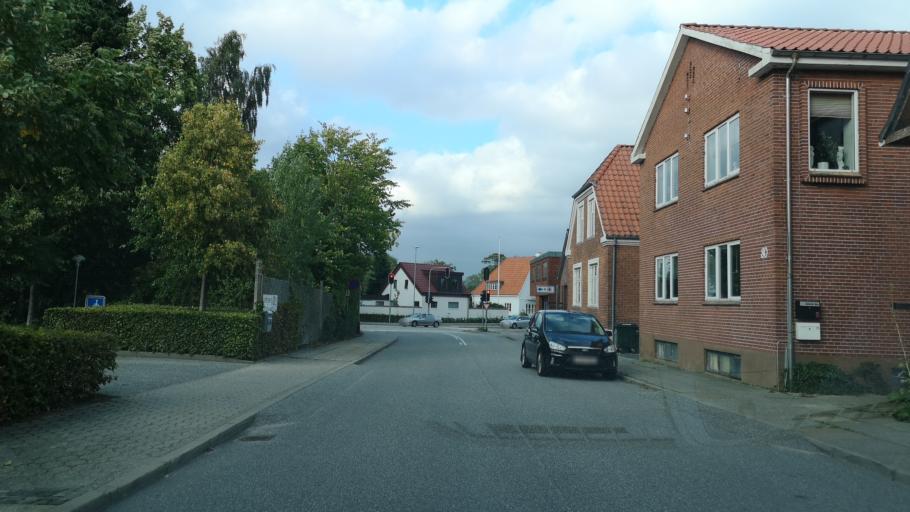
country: DK
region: Central Jutland
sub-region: Herning Kommune
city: Herning
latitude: 56.1413
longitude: 8.9753
